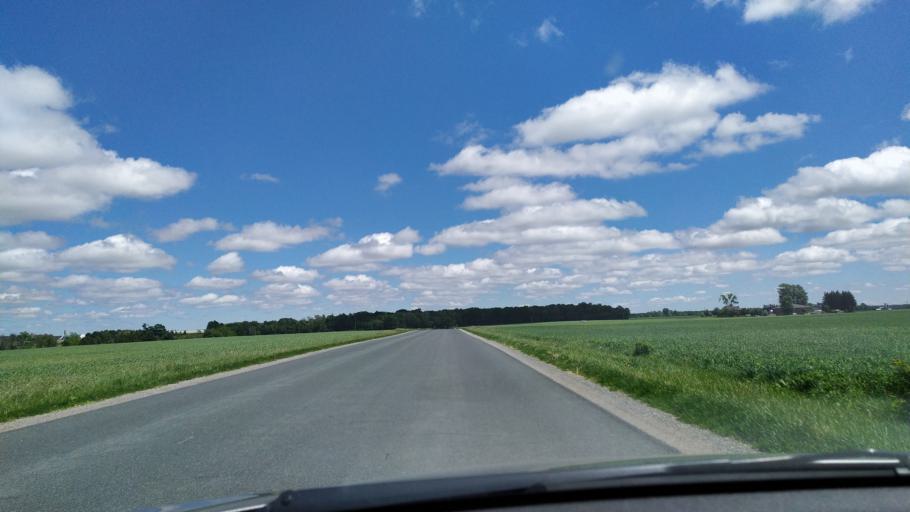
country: CA
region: Ontario
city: Huron East
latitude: 43.4535
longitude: -81.1890
